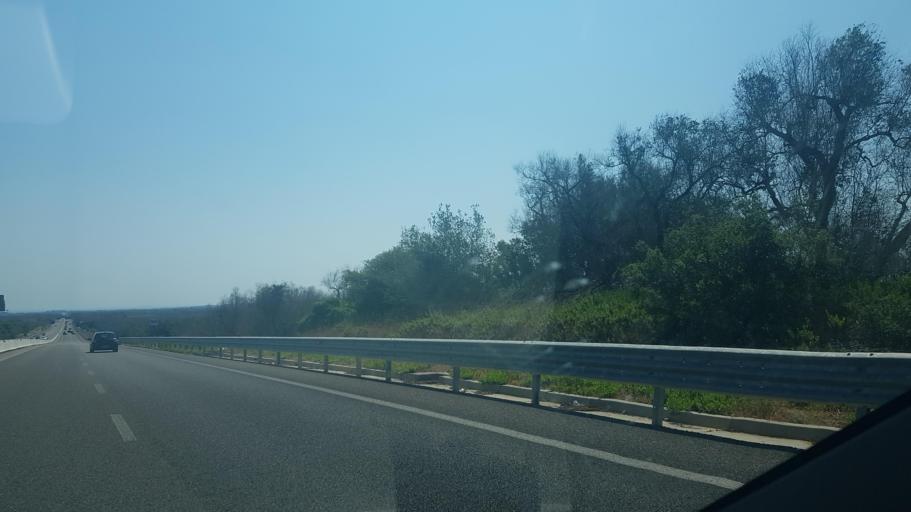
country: IT
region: Apulia
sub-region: Provincia di Lecce
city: Palmariggi
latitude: 40.1344
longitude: 18.4016
